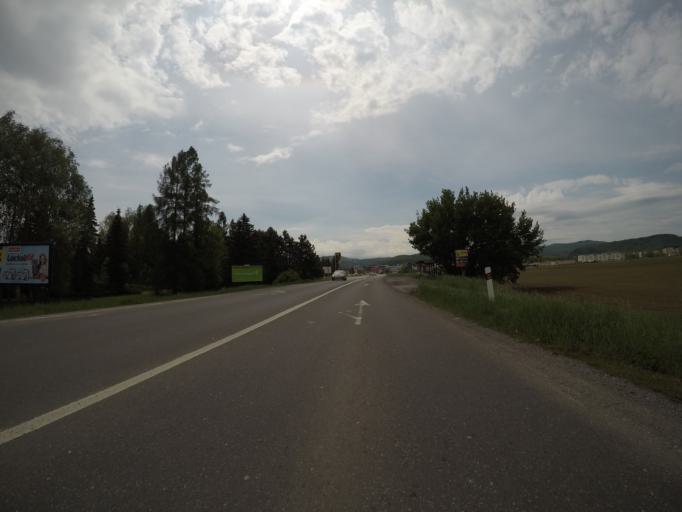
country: SK
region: Banskobystricky
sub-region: Okres Banska Bystrica
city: Zvolen
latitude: 48.5893
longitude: 19.1245
